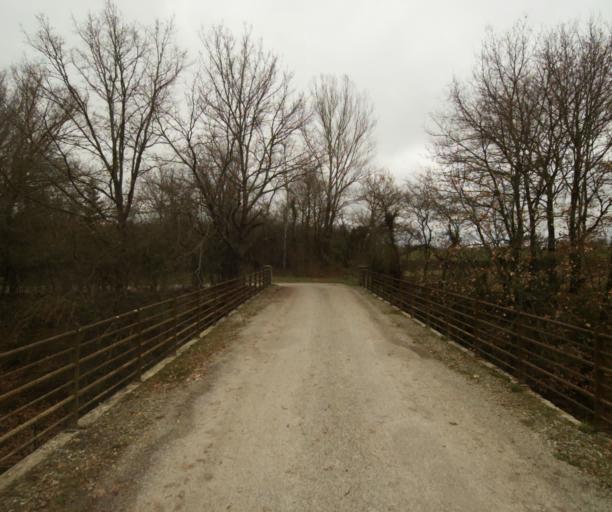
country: FR
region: Midi-Pyrenees
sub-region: Departement de l'Ariege
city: Pamiers
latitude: 43.1487
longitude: 1.5962
